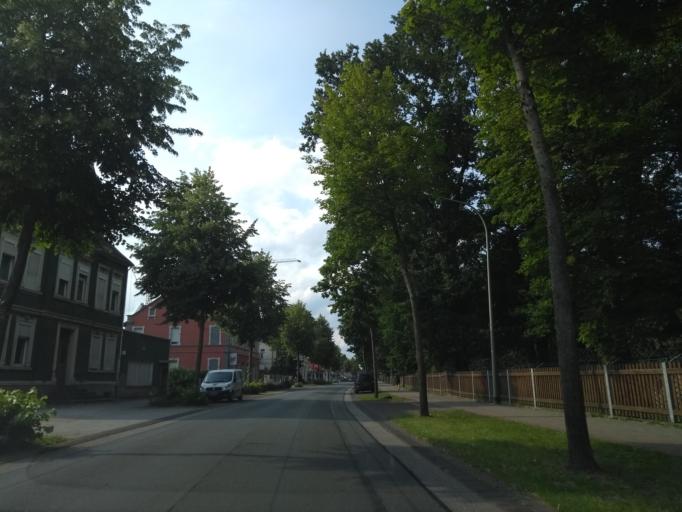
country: DE
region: North Rhine-Westphalia
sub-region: Regierungsbezirk Detmold
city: Paderborn
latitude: 51.7684
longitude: 8.7170
